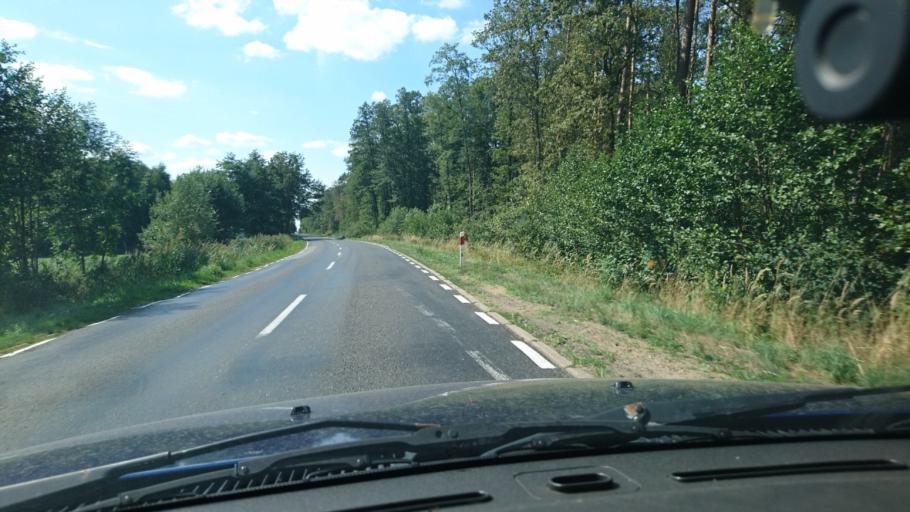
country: PL
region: Greater Poland Voivodeship
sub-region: Powiat krotoszynski
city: Sulmierzyce
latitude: 51.6016
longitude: 17.5890
